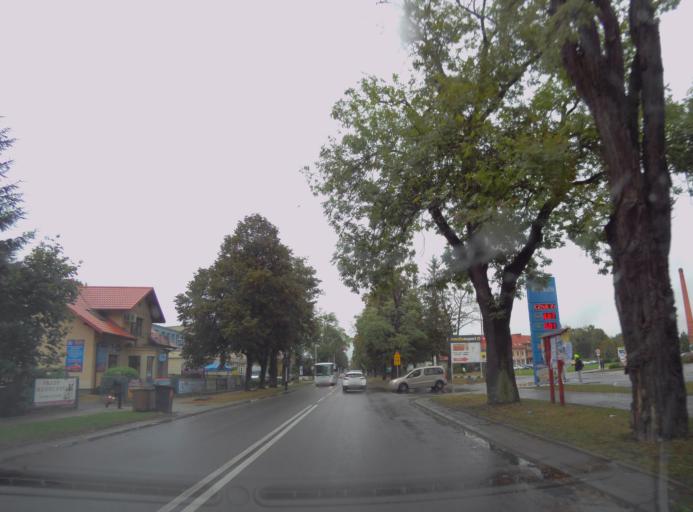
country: PL
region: Subcarpathian Voivodeship
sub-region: Powiat lezajski
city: Lezajsk
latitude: 50.2635
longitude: 22.4176
